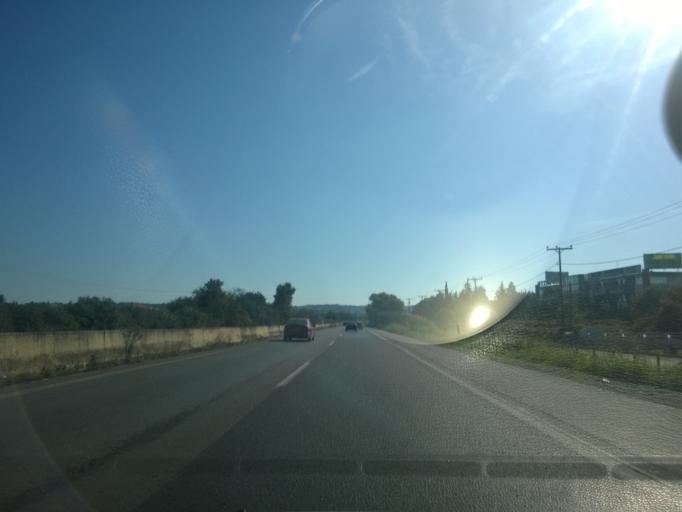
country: GR
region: Central Macedonia
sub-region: Nomos Thessalonikis
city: Neo Rysi
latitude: 40.5076
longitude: 23.0070
